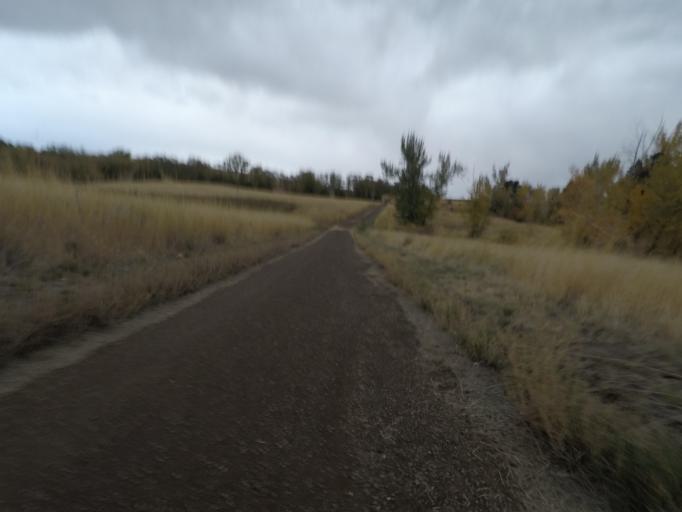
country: US
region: Washington
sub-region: Walla Walla County
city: Walla Walla East
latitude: 46.0653
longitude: -118.2565
